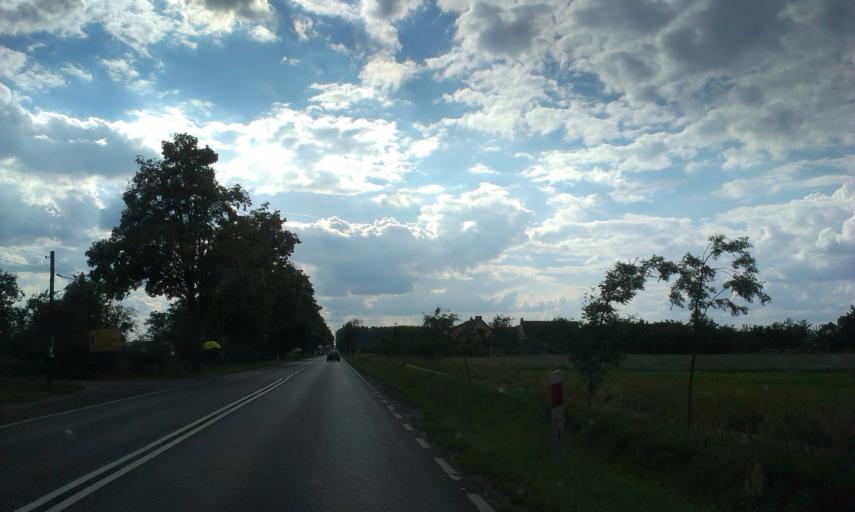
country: PL
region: Greater Poland Voivodeship
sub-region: Powiat pilski
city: Miasteczko Krajenskie
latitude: 53.1322
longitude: 17.0046
